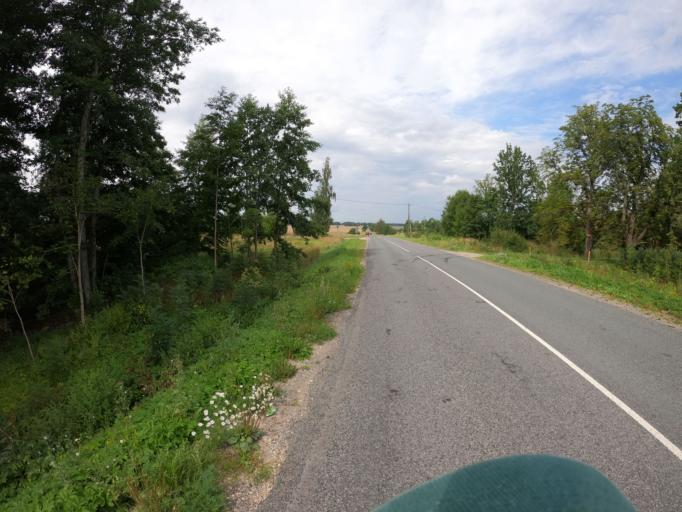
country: LV
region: Aizpute
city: Aizpute
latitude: 56.6869
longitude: 21.6409
